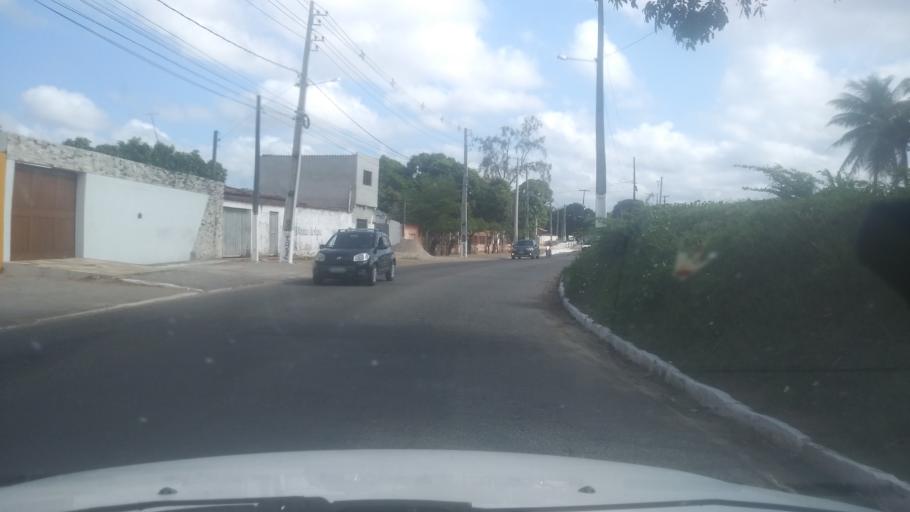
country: BR
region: Rio Grande do Norte
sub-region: Extremoz
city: Extremoz
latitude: -5.7064
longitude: -35.2812
